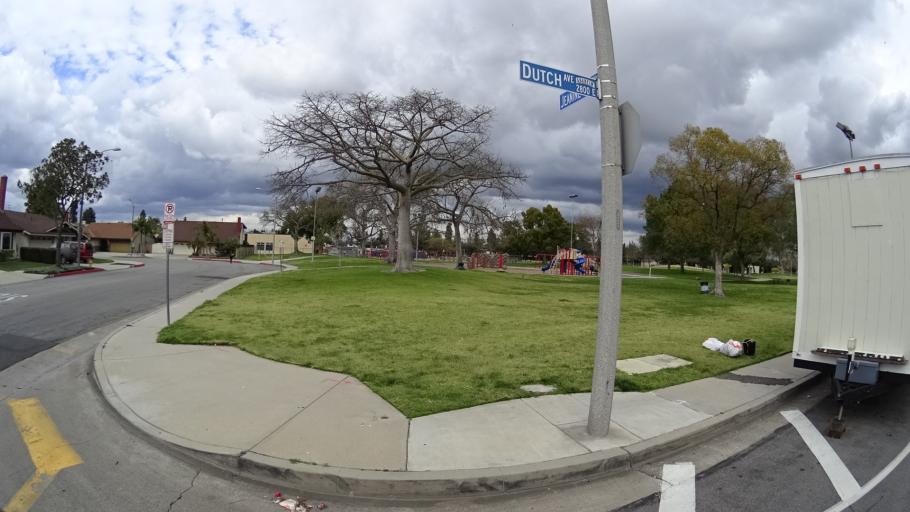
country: US
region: California
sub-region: Orange County
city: Placentia
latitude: 33.8419
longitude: -117.8693
